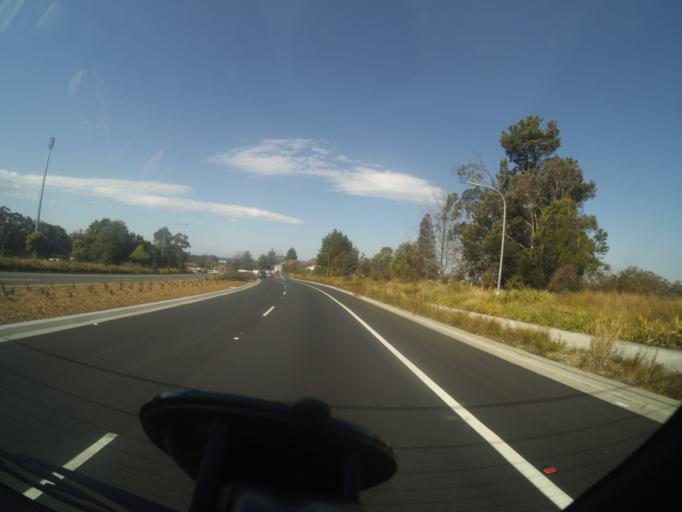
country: AU
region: New South Wales
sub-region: Blue Mountains Municipality
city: Lawson
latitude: -33.7240
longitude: 150.4201
